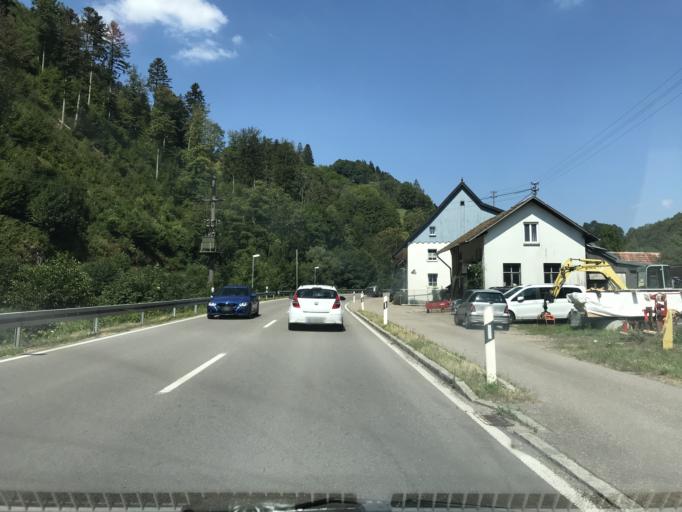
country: DE
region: Baden-Wuerttemberg
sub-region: Freiburg Region
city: Wembach
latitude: 47.7399
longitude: 7.8820
